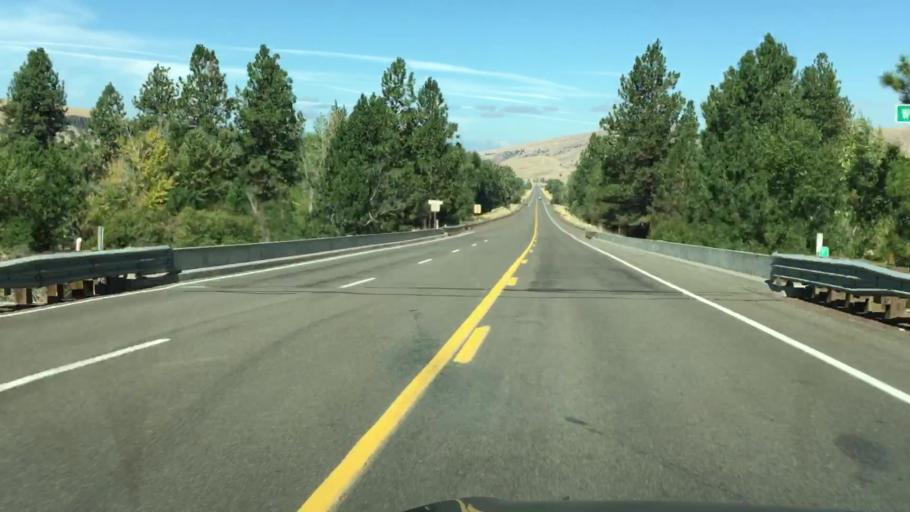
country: US
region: Oregon
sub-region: Wasco County
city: The Dalles
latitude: 45.2386
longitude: -121.1470
